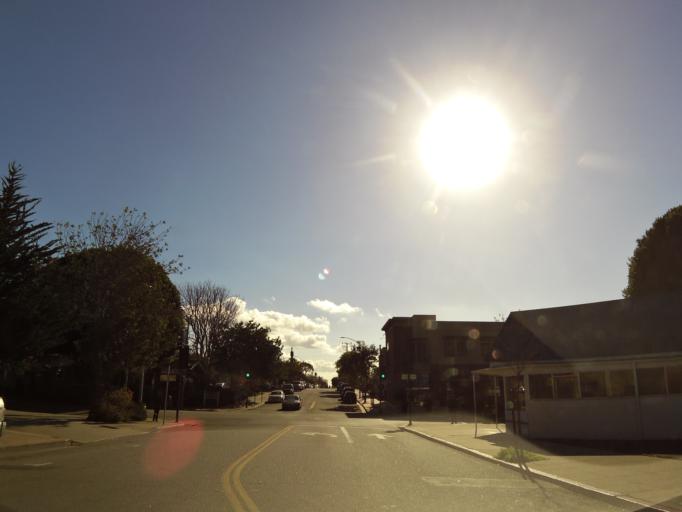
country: US
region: California
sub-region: San Luis Obispo County
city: San Luis Obispo
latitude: 35.2777
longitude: -120.6654
